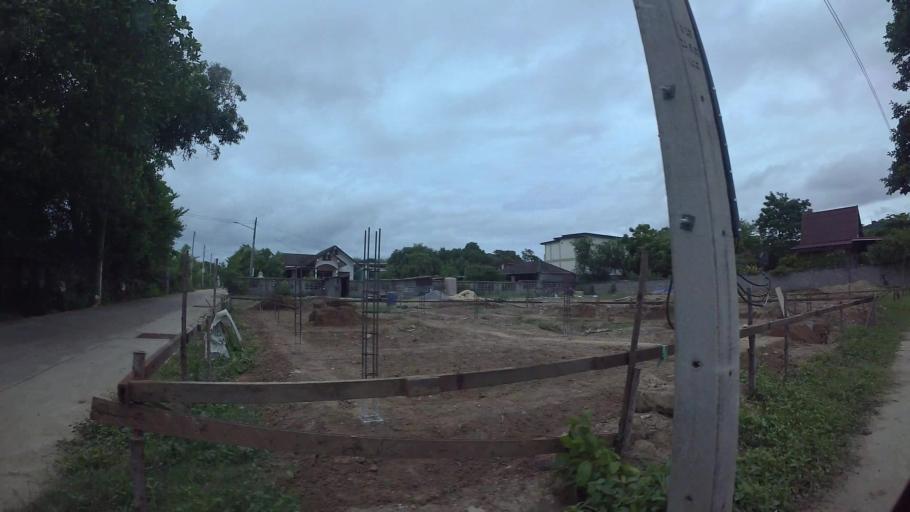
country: TH
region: Chon Buri
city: Sattahip
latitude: 12.6863
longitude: 100.9007
